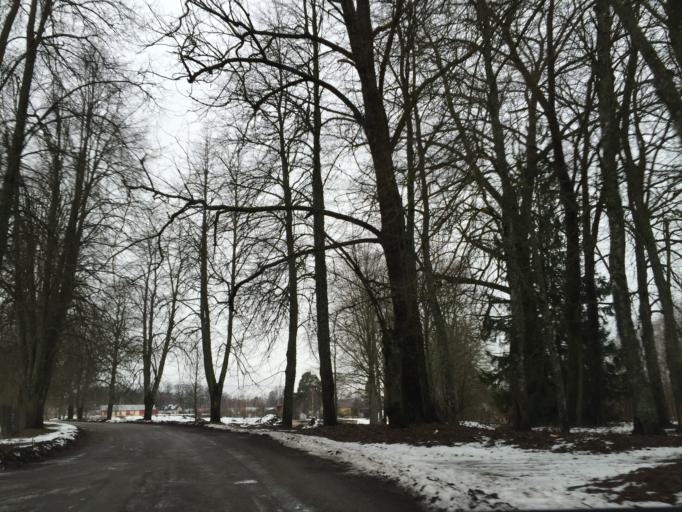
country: LV
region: Krimulda
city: Ragana
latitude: 57.1839
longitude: 24.7179
